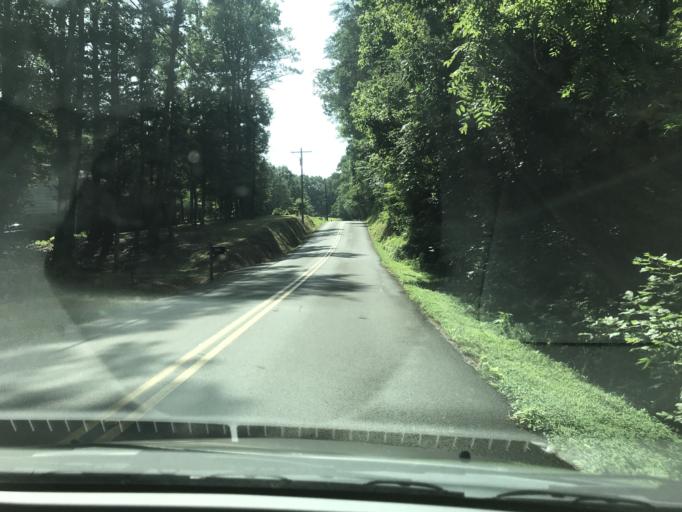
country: US
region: Tennessee
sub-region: Hamilton County
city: Apison
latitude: 35.0703
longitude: -84.9816
